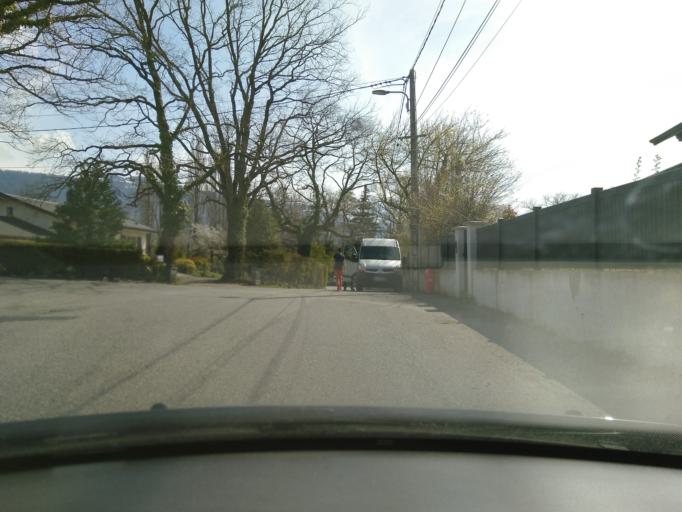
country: FR
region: Rhone-Alpes
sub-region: Departement de la Haute-Savoie
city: Neydens
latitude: 46.1382
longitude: 6.1083
